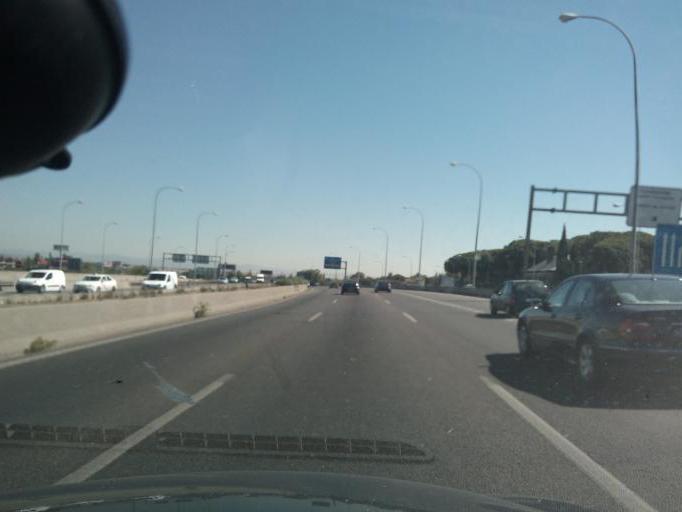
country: ES
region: Madrid
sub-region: Provincia de Madrid
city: Las Tablas
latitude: 40.5145
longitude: -3.6548
